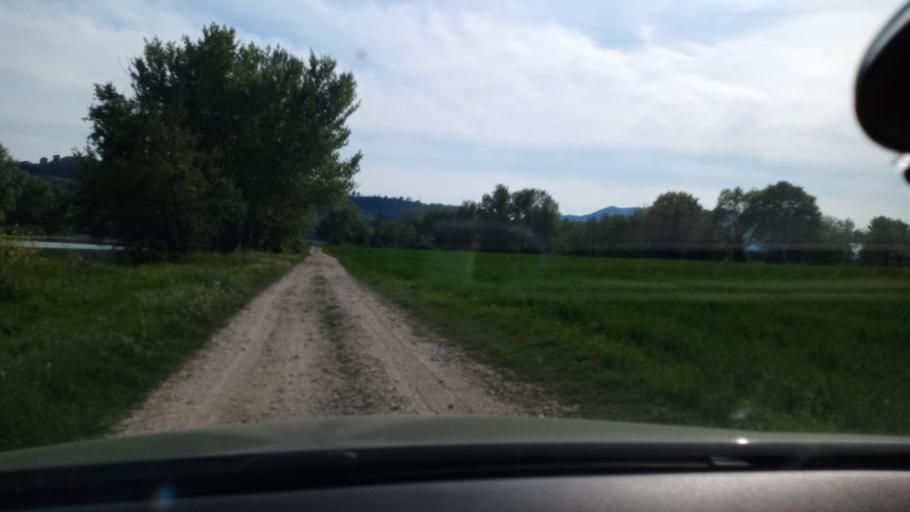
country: IT
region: Latium
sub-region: Citta metropolitana di Roma Capitale
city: Ponzano Romano
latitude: 42.2755
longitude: 12.5785
